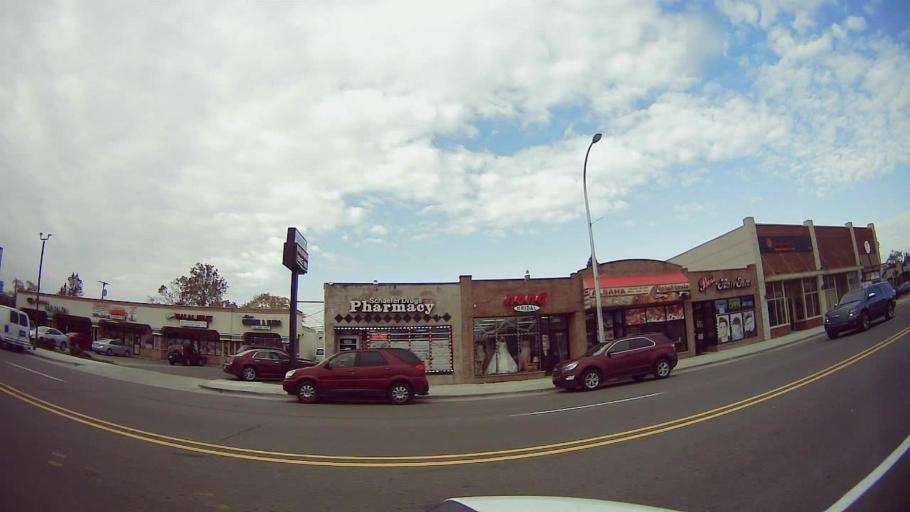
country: US
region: Michigan
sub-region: Wayne County
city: Dearborn
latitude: 42.3399
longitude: -83.1766
